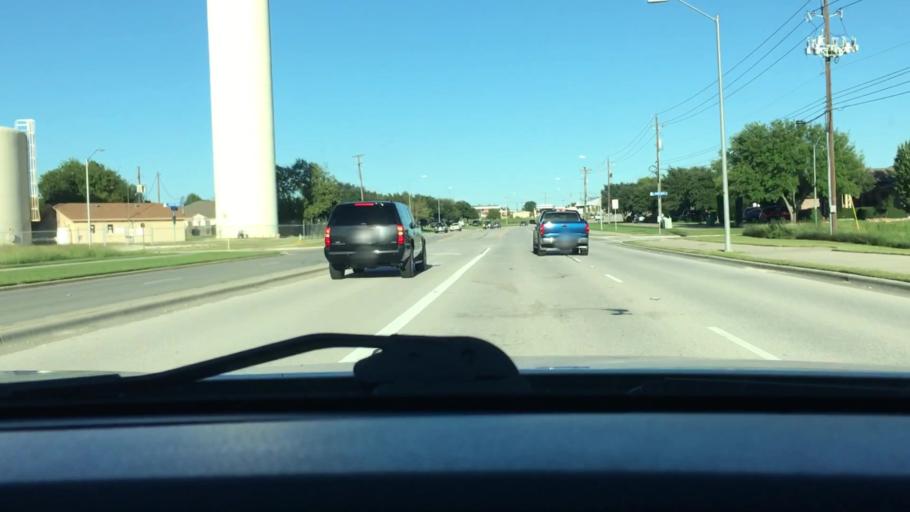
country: US
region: Texas
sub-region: Travis County
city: Windemere
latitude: 30.4720
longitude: -97.6466
